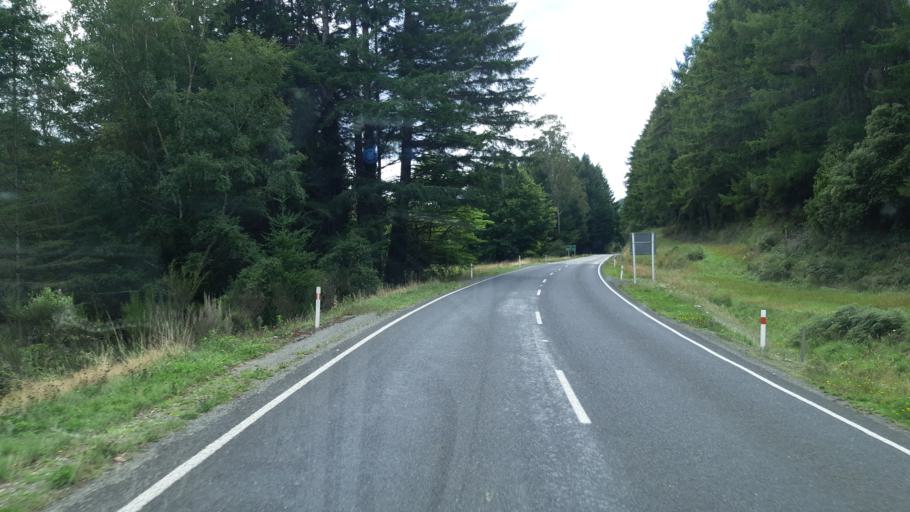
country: NZ
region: Tasman
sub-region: Tasman District
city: Wakefield
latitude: -41.6026
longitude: 172.7586
